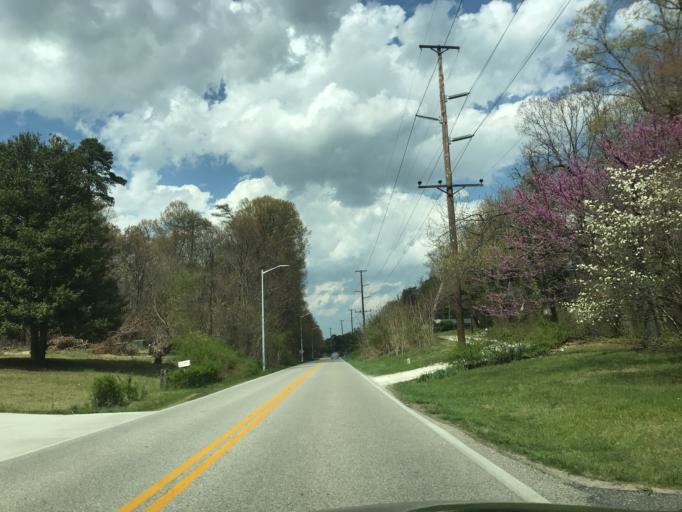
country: US
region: Maryland
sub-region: Anne Arundel County
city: Severn
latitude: 39.1284
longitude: -76.6753
